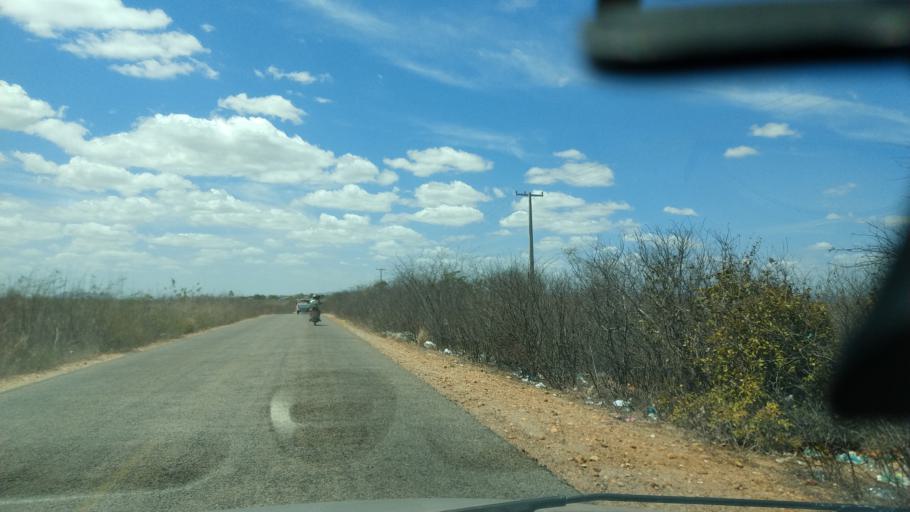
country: BR
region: Rio Grande do Norte
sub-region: Sao Paulo Do Potengi
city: Sao Paulo do Potengi
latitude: -5.9144
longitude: -35.7436
